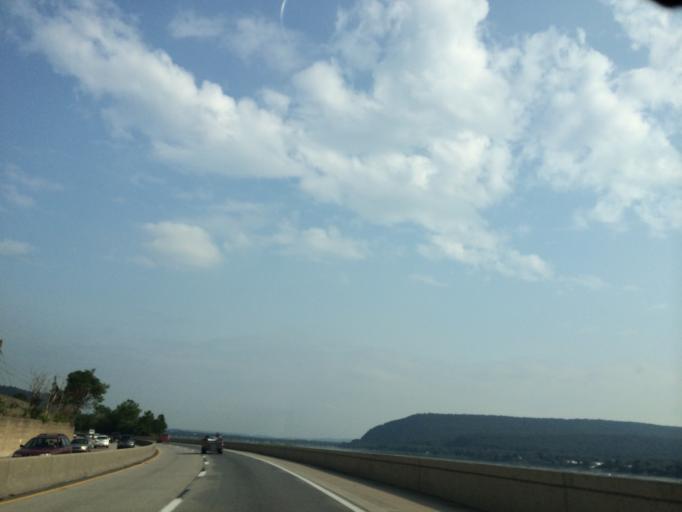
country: US
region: Pennsylvania
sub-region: Perry County
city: Marysville
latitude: 40.3578
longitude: -76.9243
